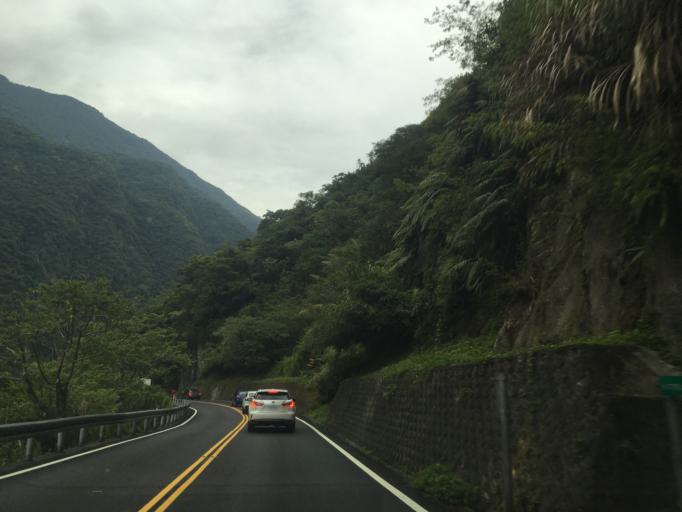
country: TW
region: Taiwan
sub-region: Hualien
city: Hualian
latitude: 24.1740
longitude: 121.5805
